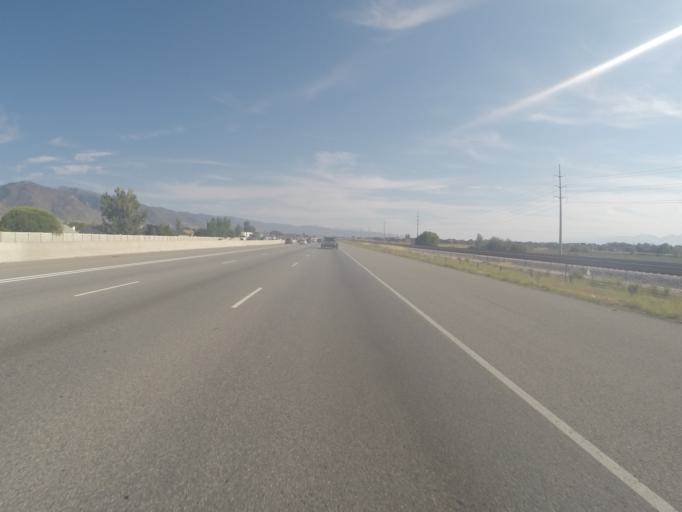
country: US
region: Utah
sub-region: Davis County
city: Kaysville
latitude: 41.0282
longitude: -111.9469
